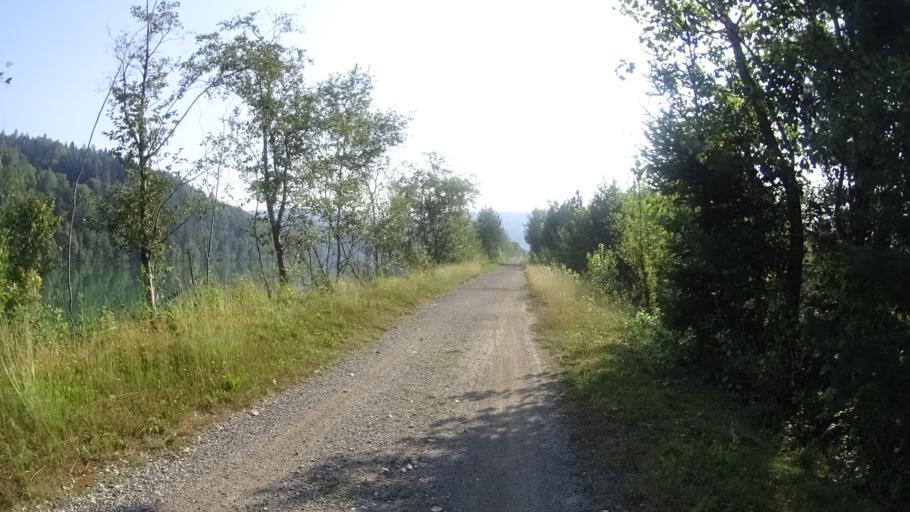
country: AT
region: Carinthia
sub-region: Politischer Bezirk Klagenfurt Land
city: Maria Rain
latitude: 46.5445
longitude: 14.2730
